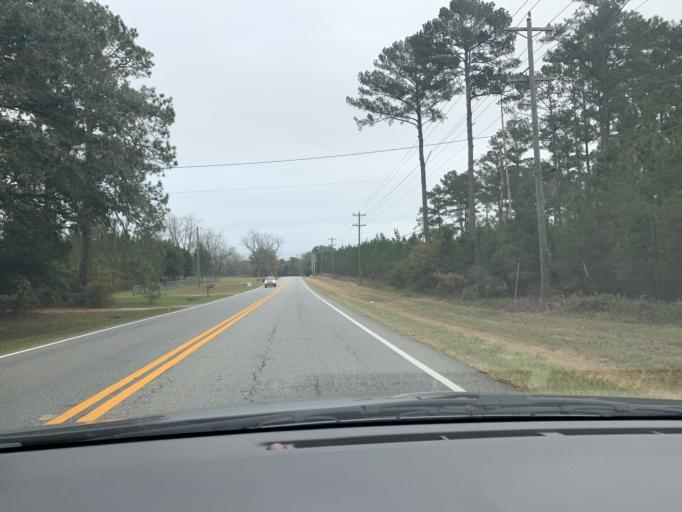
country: US
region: Georgia
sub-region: Thomas County
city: Thomasville
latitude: 30.8580
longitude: -83.9180
